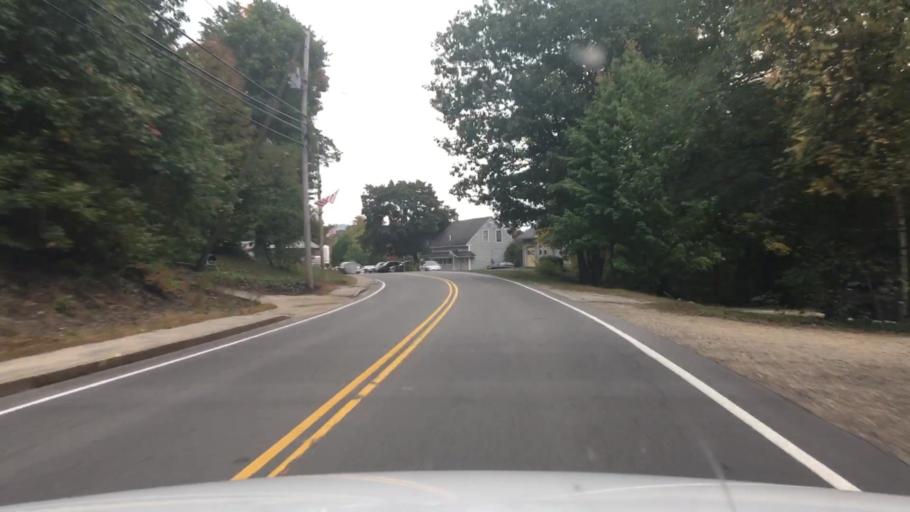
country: US
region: New Hampshire
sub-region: Strafford County
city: New Durham
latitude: 43.4612
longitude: -71.2270
